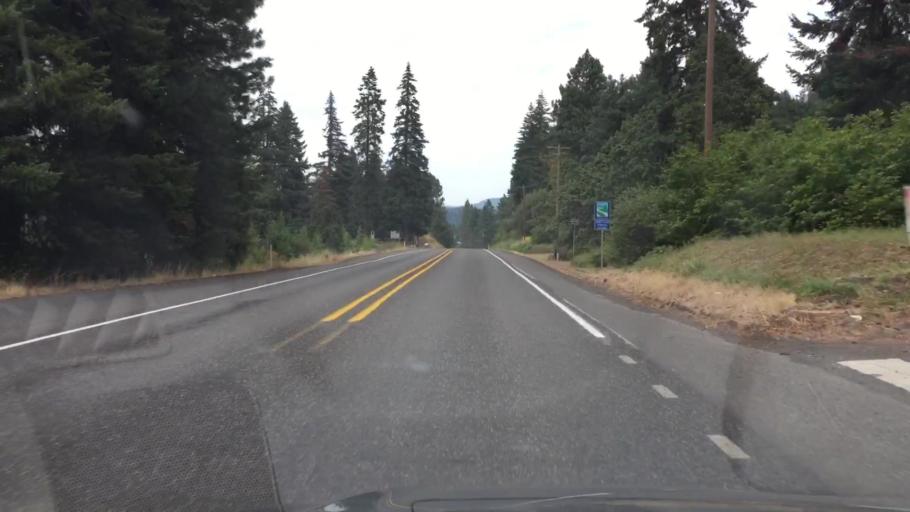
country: US
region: Washington
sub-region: Klickitat County
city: White Salmon
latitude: 45.7865
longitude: -121.4997
